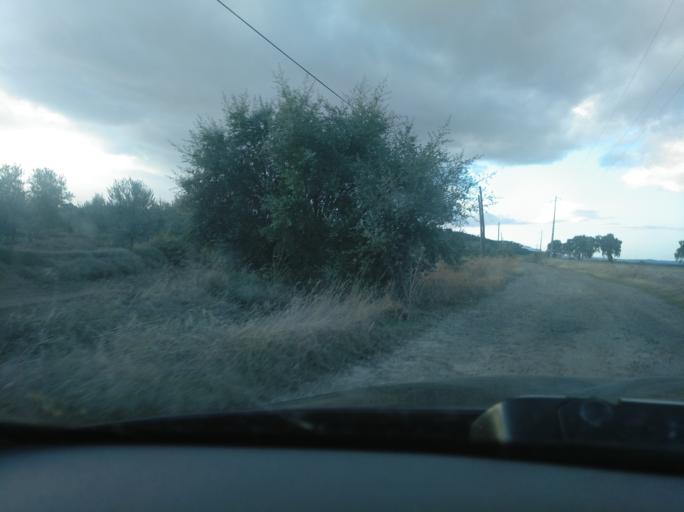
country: PT
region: Portalegre
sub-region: Campo Maior
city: Campo Maior
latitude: 39.0409
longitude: -6.9912
